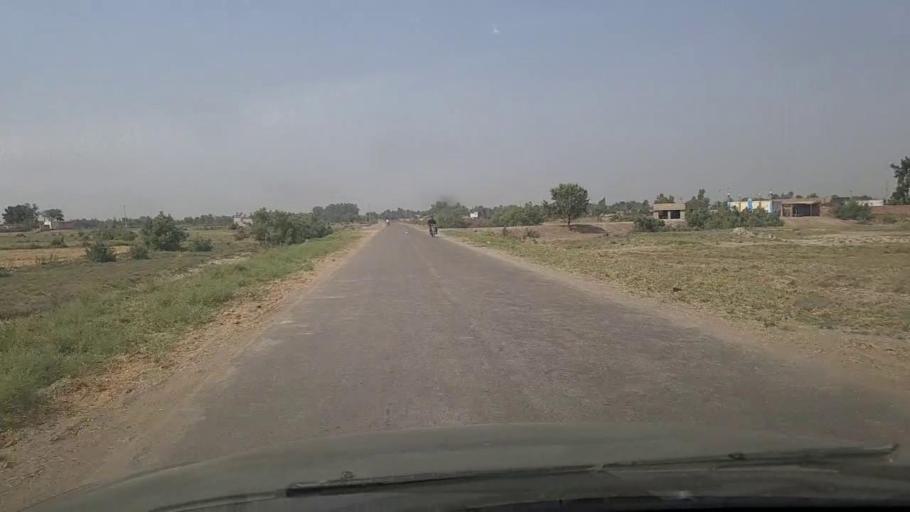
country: PK
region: Sindh
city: Khanpur
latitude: 27.8970
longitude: 69.4914
